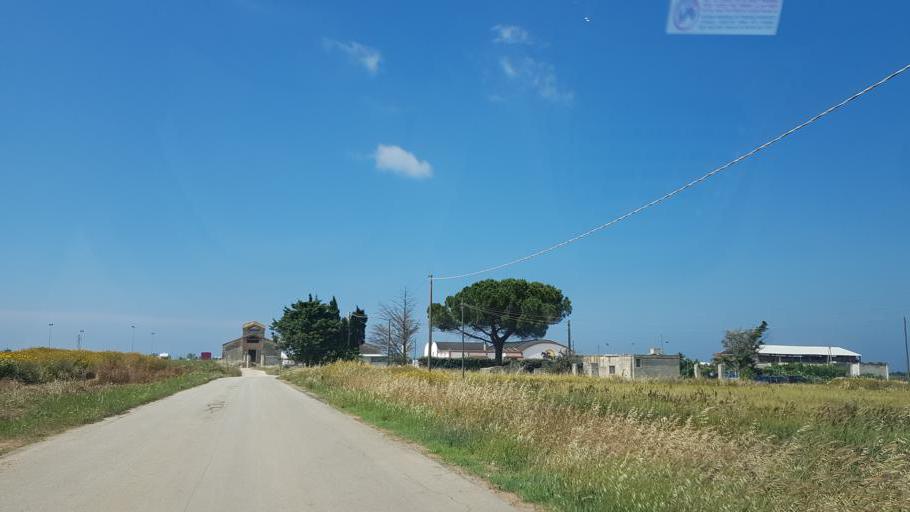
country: IT
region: Apulia
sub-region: Provincia di Brindisi
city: Brindisi
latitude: 40.6591
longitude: 17.8515
